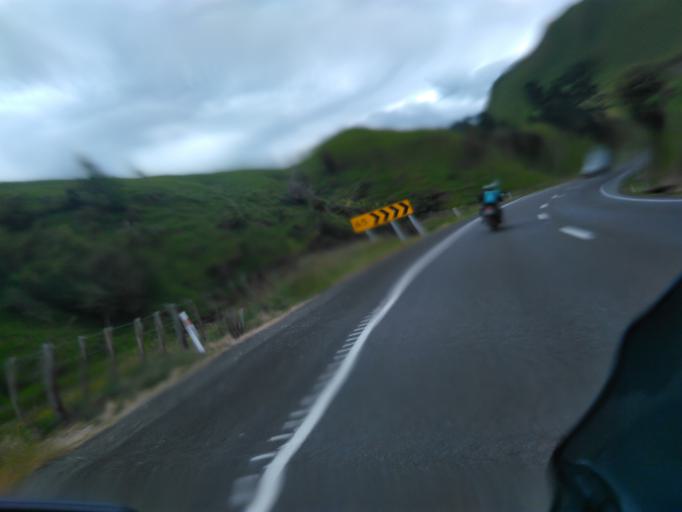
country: NZ
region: Bay of Plenty
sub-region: Opotiki District
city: Opotiki
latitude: -38.3714
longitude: 177.4652
